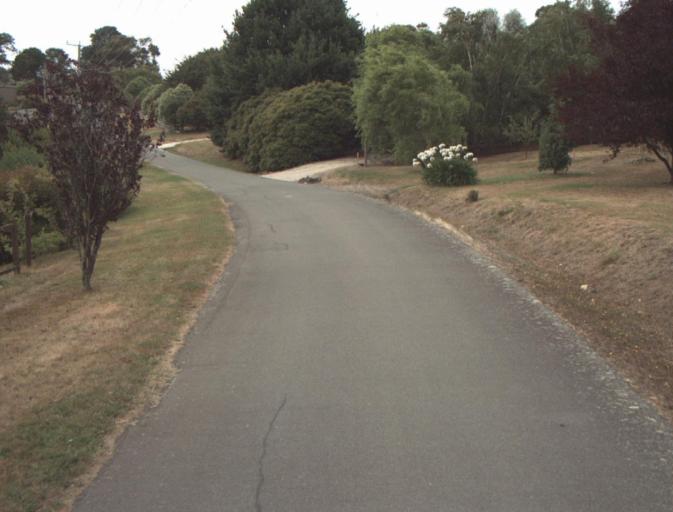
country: AU
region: Tasmania
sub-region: Launceston
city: Mayfield
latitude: -41.3277
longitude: 147.0659
